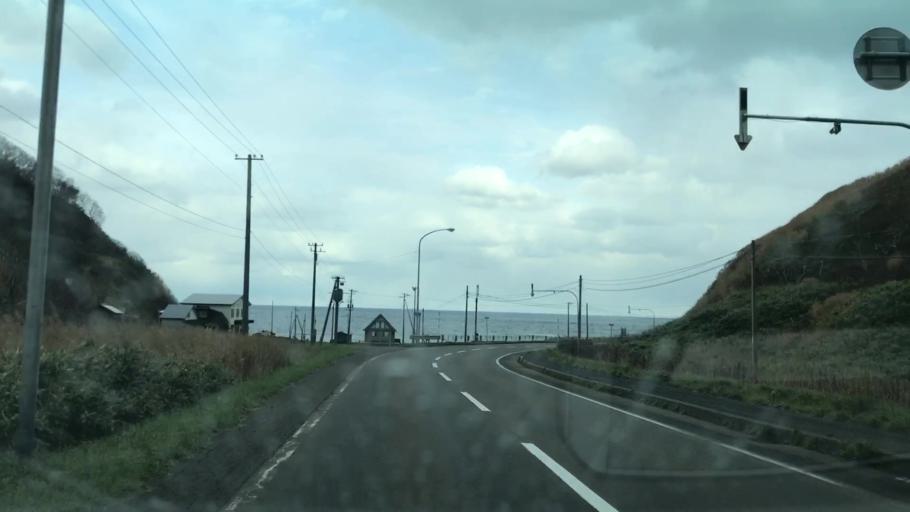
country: JP
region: Hokkaido
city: Iwanai
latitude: 43.3283
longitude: 140.3655
